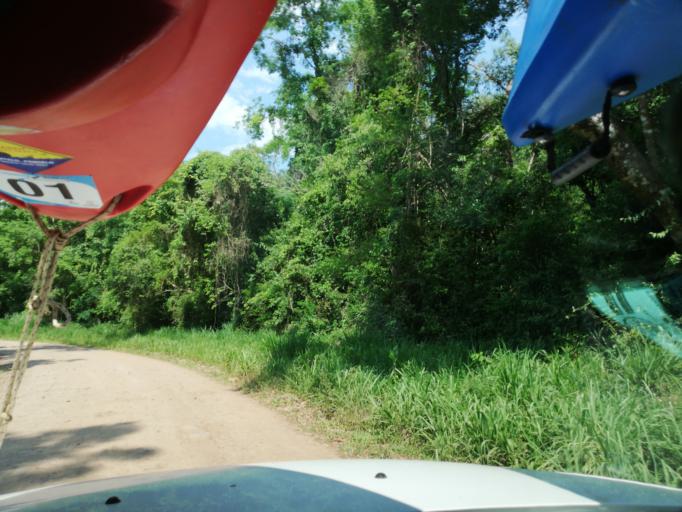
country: AR
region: Misiones
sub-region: Departamento de San Ignacio
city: San Ignacio
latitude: -27.2701
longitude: -55.5544
